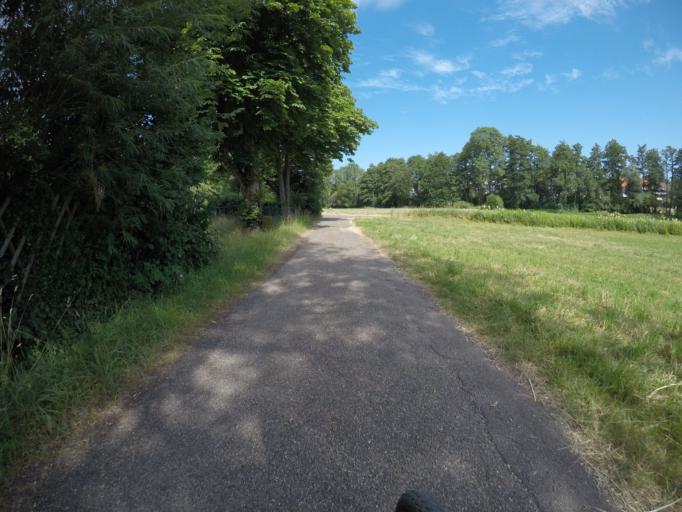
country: DE
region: Baden-Wuerttemberg
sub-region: Regierungsbezirk Stuttgart
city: Steinenbronn
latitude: 48.7275
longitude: 9.0919
